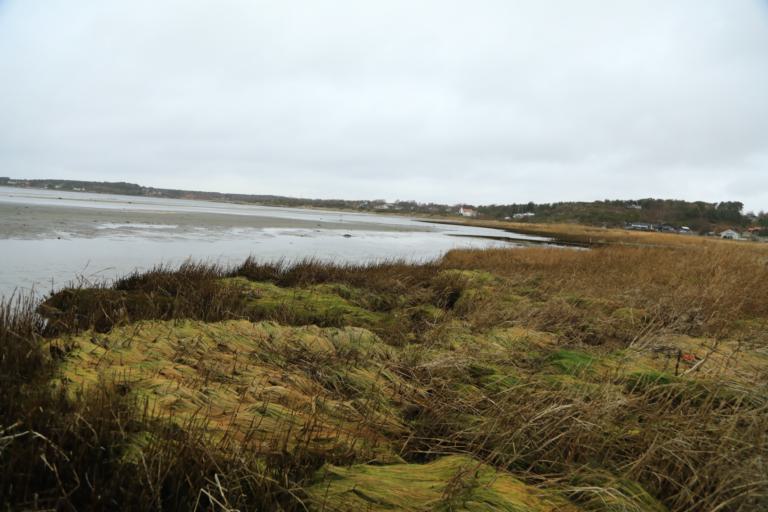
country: SE
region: Halland
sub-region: Varbergs Kommun
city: Varberg
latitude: 57.1814
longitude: 12.2132
